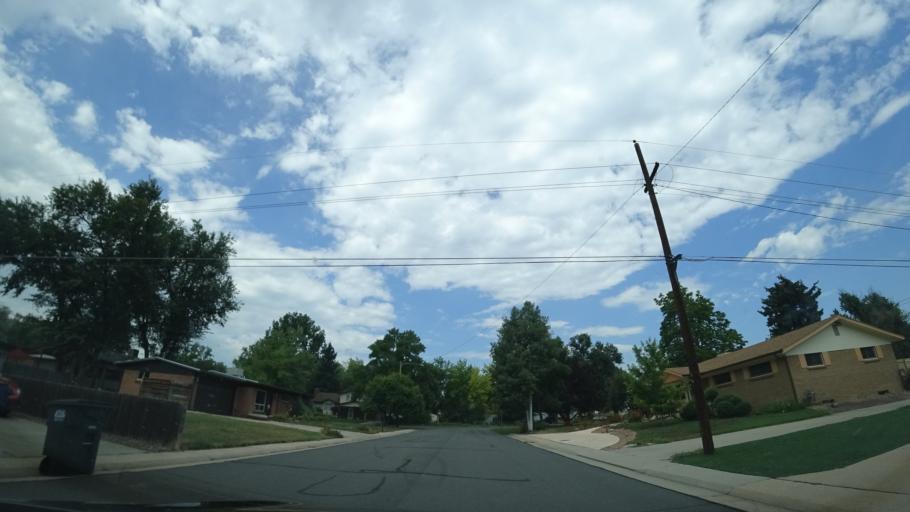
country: US
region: Colorado
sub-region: Jefferson County
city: Lakewood
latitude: 39.7222
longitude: -105.0749
